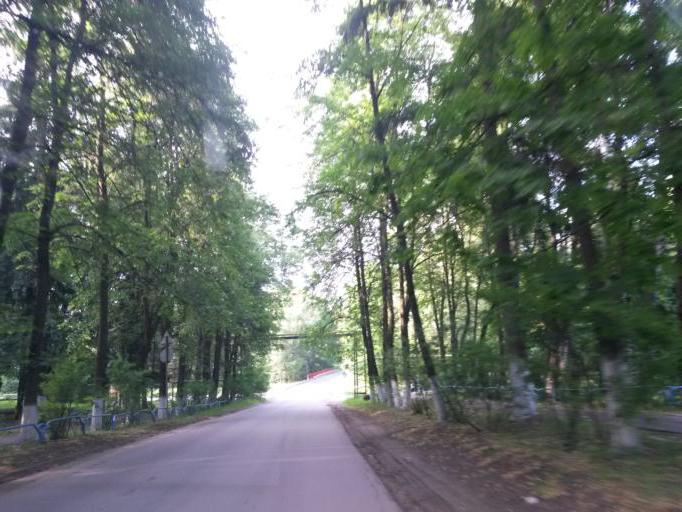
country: RU
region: Moskovskaya
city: Lyubuchany
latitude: 55.2435
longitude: 37.5442
